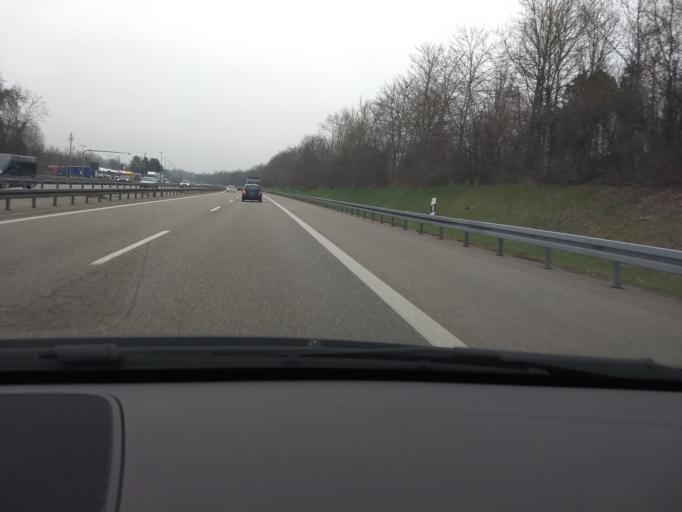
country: DE
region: Baden-Wuerttemberg
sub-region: Freiburg Region
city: Bad Bellingen
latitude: 47.7346
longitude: 7.5520
